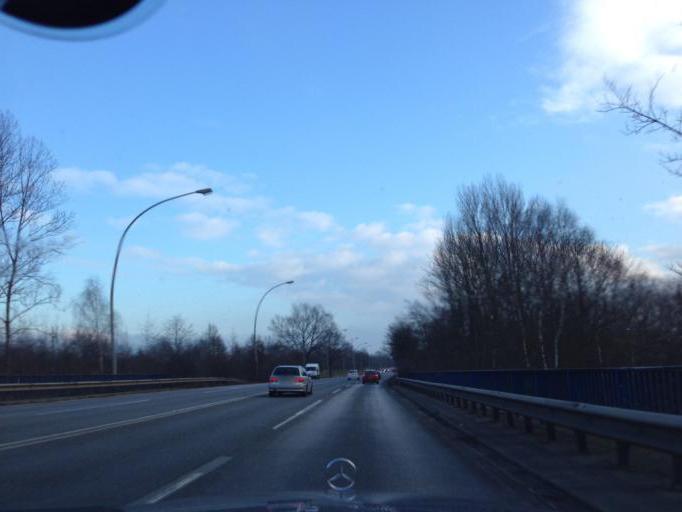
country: DE
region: Schleswig-Holstein
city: Oststeinbek
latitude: 53.5219
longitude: 10.1476
